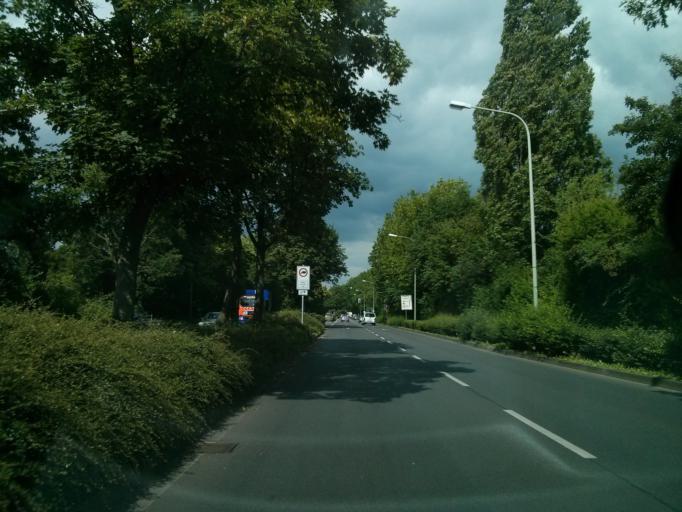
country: DE
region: North Rhine-Westphalia
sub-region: Regierungsbezirk Dusseldorf
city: Krefeld
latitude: 51.3463
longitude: 6.5628
